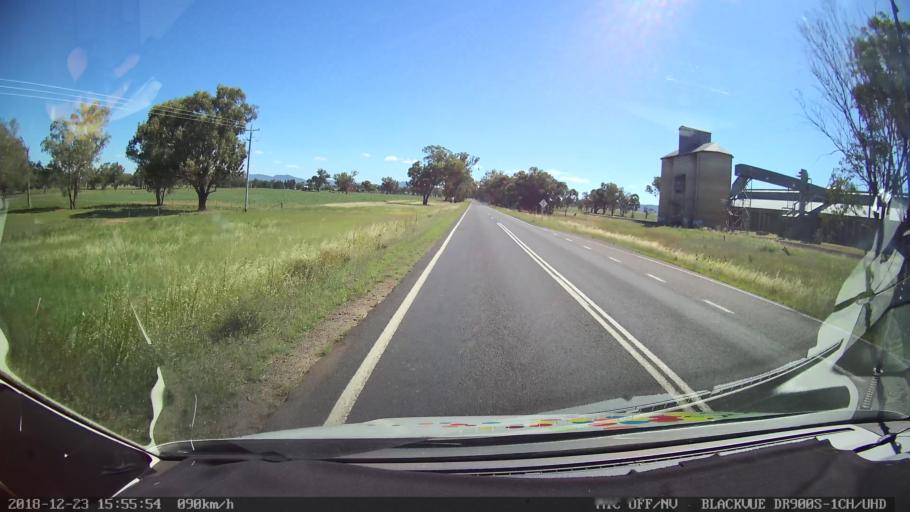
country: AU
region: New South Wales
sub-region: Tamworth Municipality
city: Phillip
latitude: -31.1602
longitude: 150.8637
